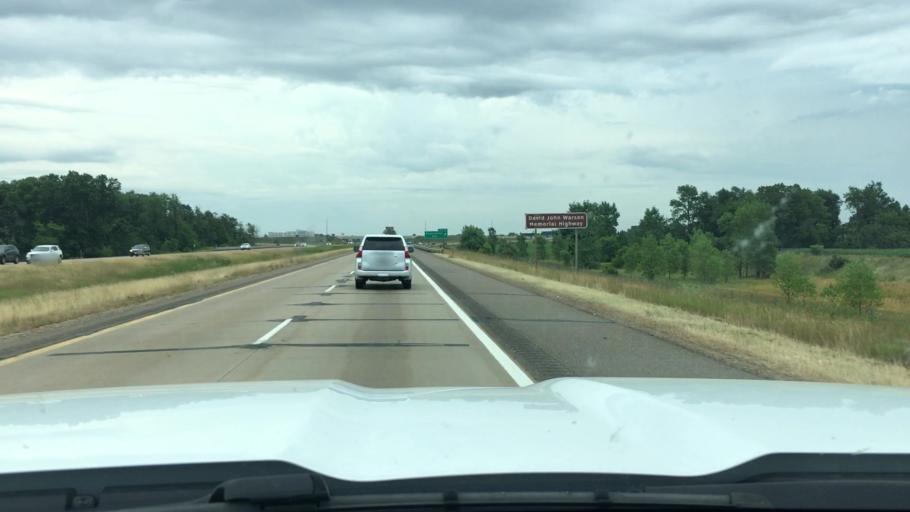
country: US
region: Michigan
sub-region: Kent County
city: Byron Center
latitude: 42.8526
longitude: -85.7359
